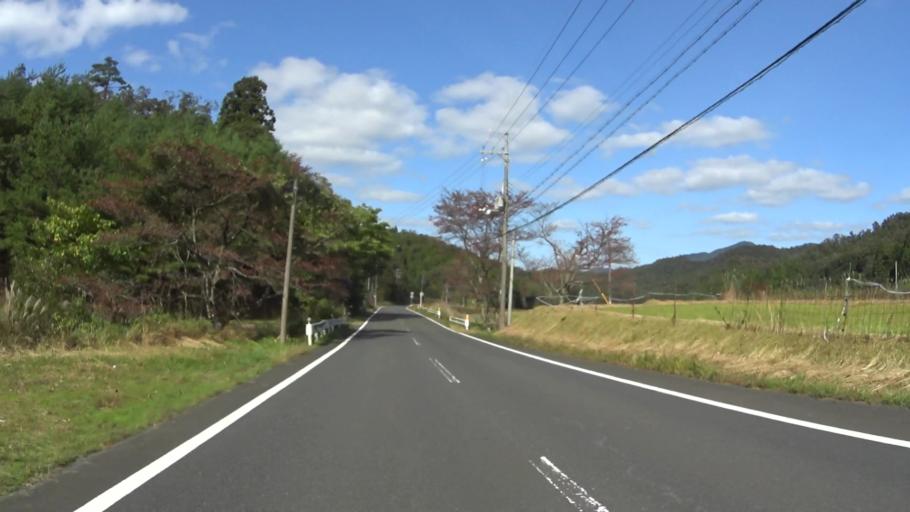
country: JP
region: Hyogo
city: Toyooka
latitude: 35.5511
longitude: 134.9773
